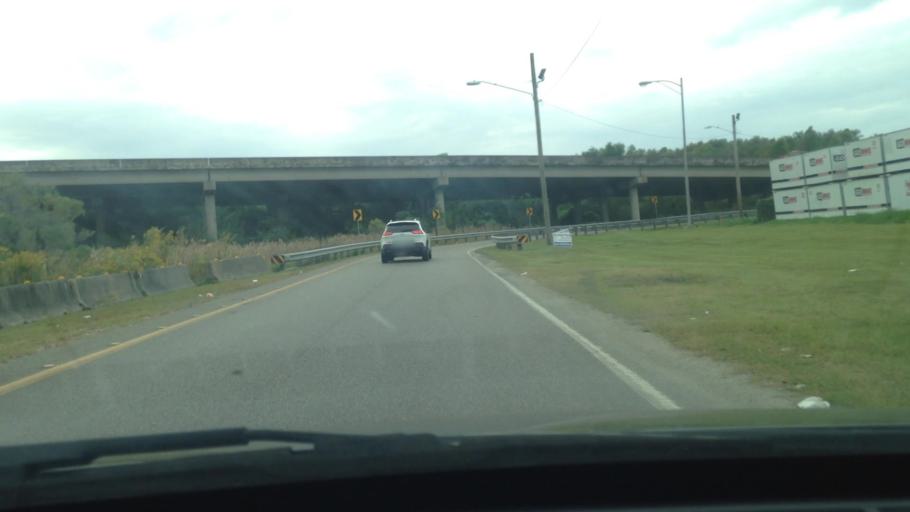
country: US
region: Louisiana
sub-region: Jefferson Parish
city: Jefferson
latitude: 29.9702
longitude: -90.1332
